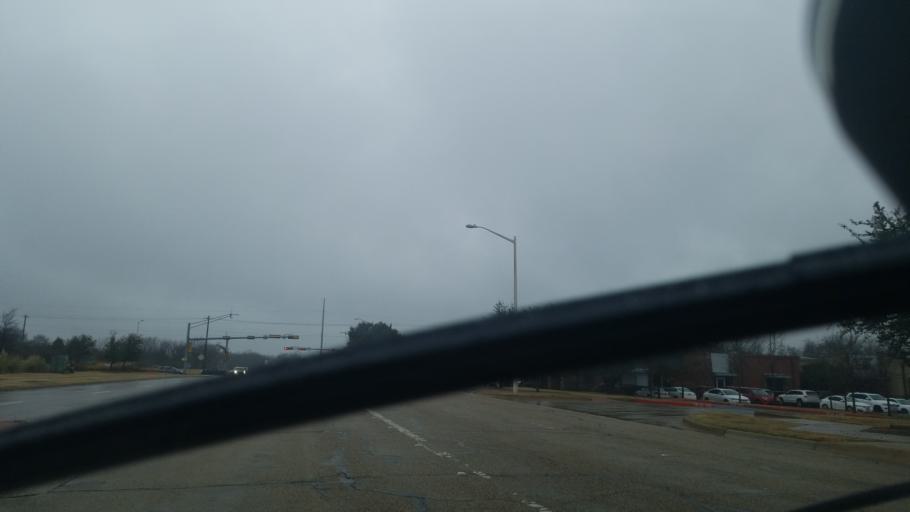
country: US
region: Texas
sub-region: Denton County
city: Denton
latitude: 33.2047
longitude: -97.0893
